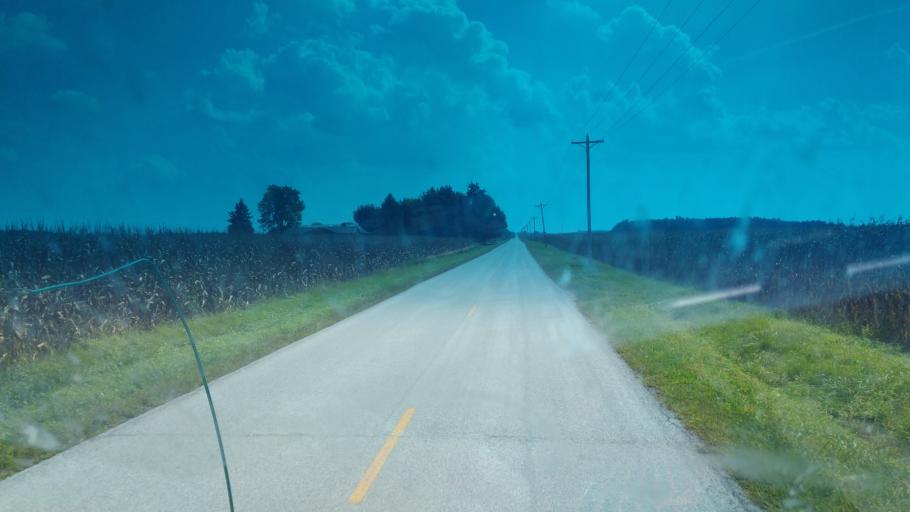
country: US
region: Ohio
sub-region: Hardin County
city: Kenton
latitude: 40.6634
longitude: -83.7271
